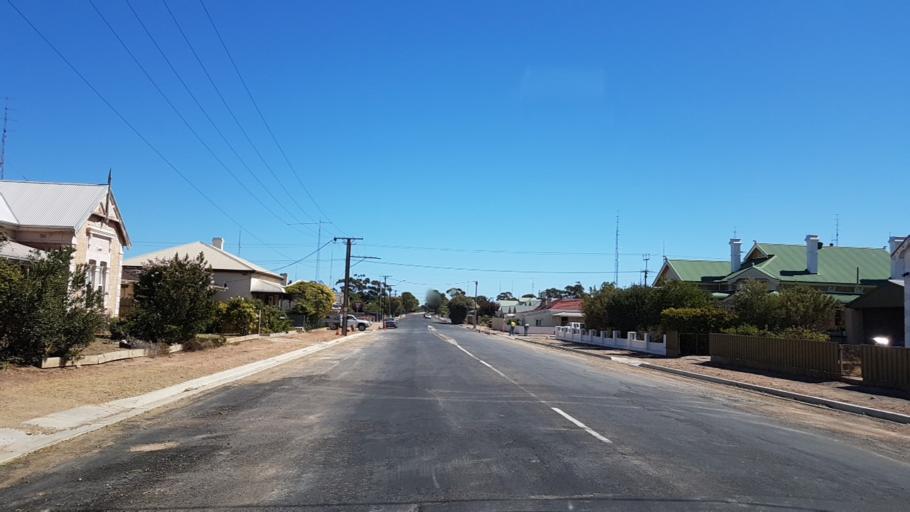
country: AU
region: South Australia
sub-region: Copper Coast
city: Kadina
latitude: -33.9615
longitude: 137.7143
